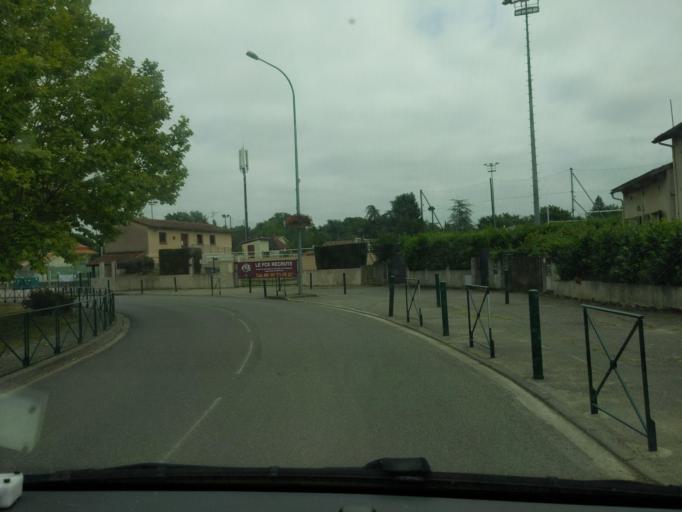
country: FR
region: Midi-Pyrenees
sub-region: Departement de la Haute-Garonne
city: Escalquens
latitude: 43.5175
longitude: 1.5579
